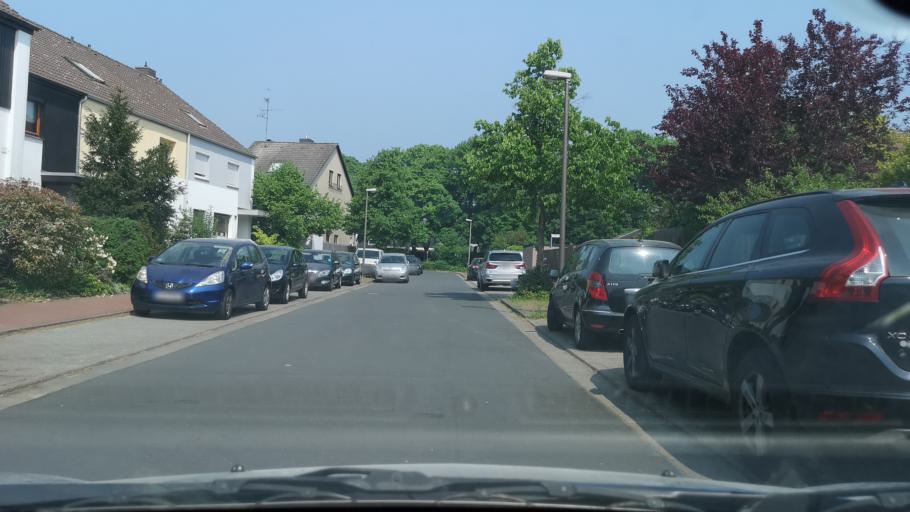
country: DE
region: Lower Saxony
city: Langenhagen
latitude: 52.4434
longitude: 9.7561
